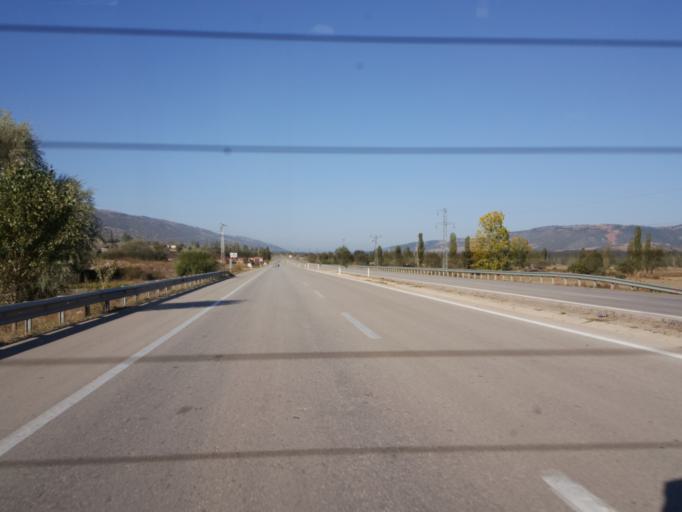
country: TR
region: Amasya
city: Ezinepazari
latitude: 40.5703
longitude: 36.0930
